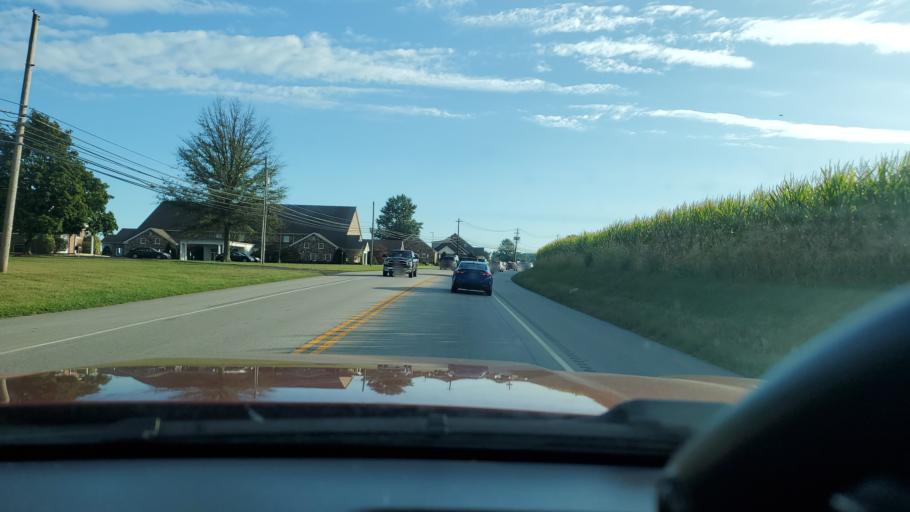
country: US
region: Pennsylvania
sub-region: Montgomery County
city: Harleysville
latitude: 40.3031
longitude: -75.3668
